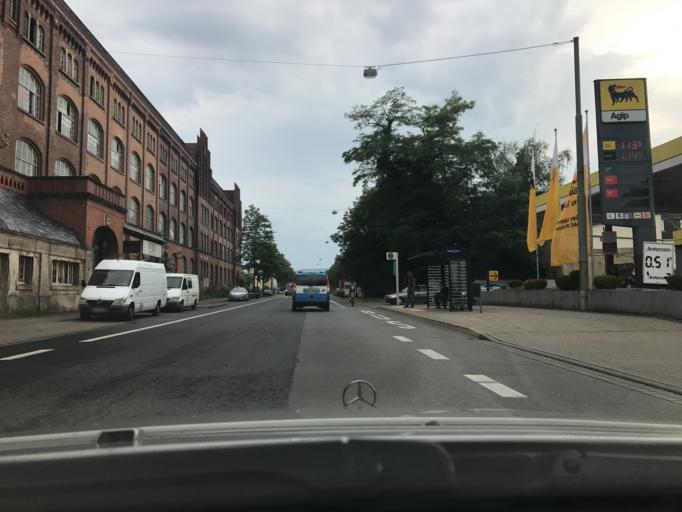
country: DE
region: Hesse
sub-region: Regierungsbezirk Kassel
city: Kassel
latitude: 51.3101
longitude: 9.5248
